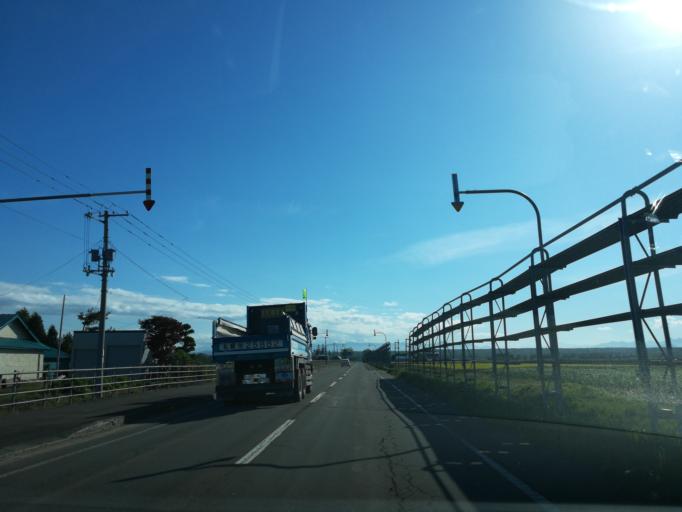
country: JP
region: Hokkaido
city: Kitahiroshima
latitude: 43.0428
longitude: 141.5886
